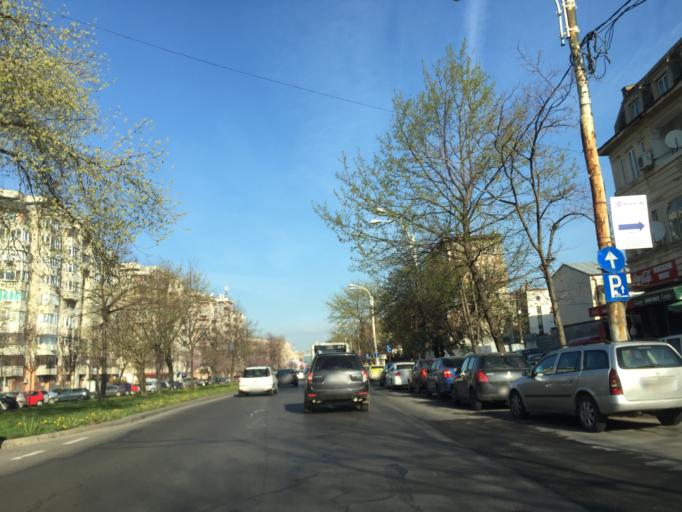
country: RO
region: Bucuresti
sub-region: Municipiul Bucuresti
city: Bucuresti
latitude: 44.4259
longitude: 26.0697
